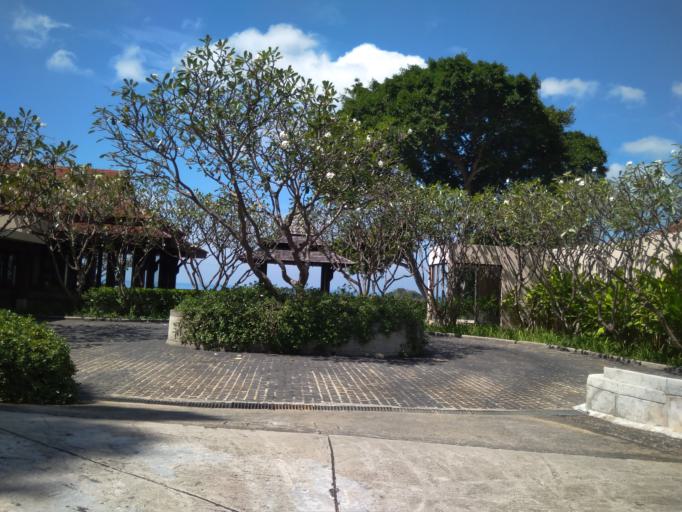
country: TH
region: Krabi
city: Ko Lanta
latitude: 7.4973
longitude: 99.0784
